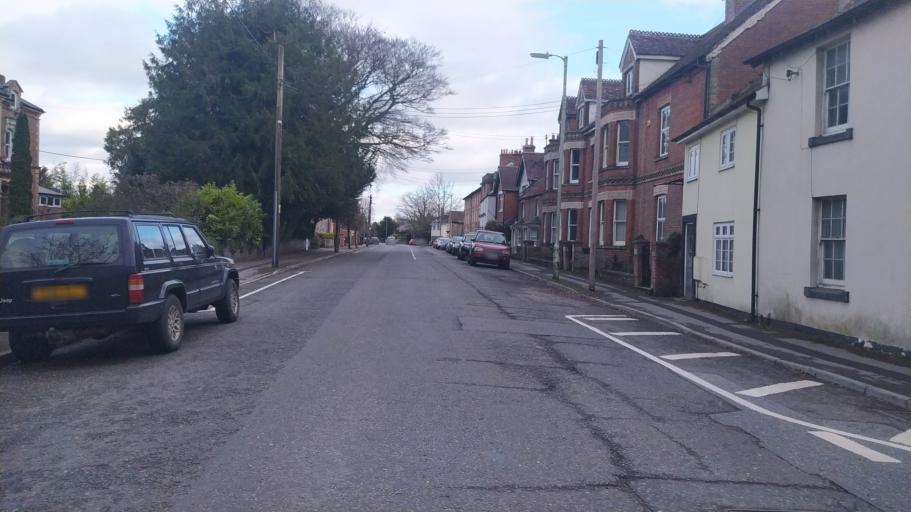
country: GB
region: England
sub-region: Wiltshire
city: Warminster
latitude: 51.2023
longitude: -2.1747
